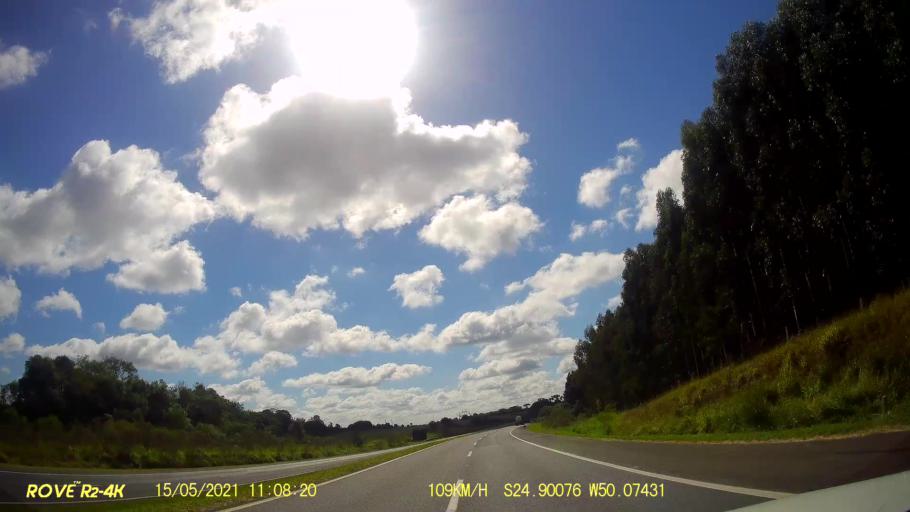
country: BR
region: Parana
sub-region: Carambei
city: Carambei
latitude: -24.9010
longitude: -50.0744
